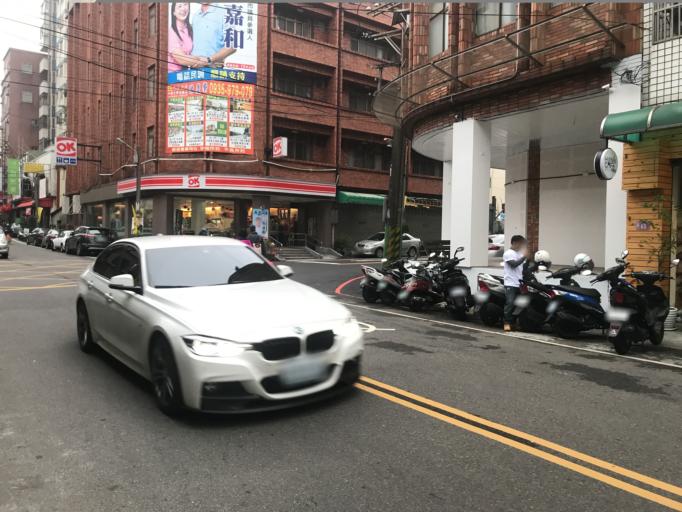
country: TW
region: Taiwan
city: Taoyuan City
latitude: 24.9522
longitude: 121.2373
